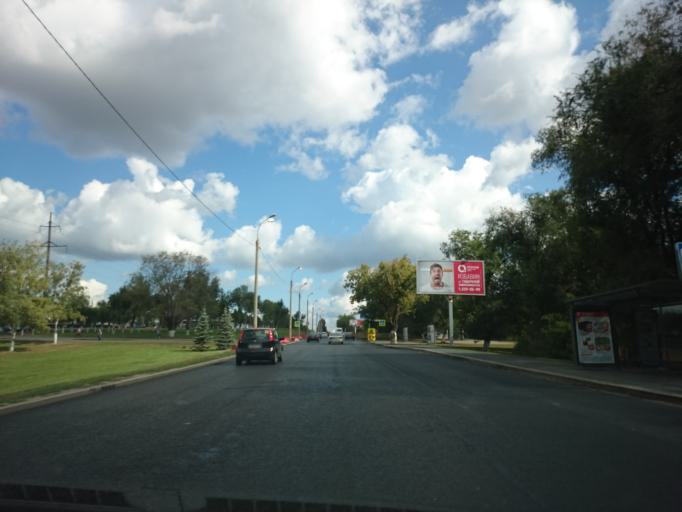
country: RU
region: Samara
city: Samara
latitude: 53.2264
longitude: 50.1741
